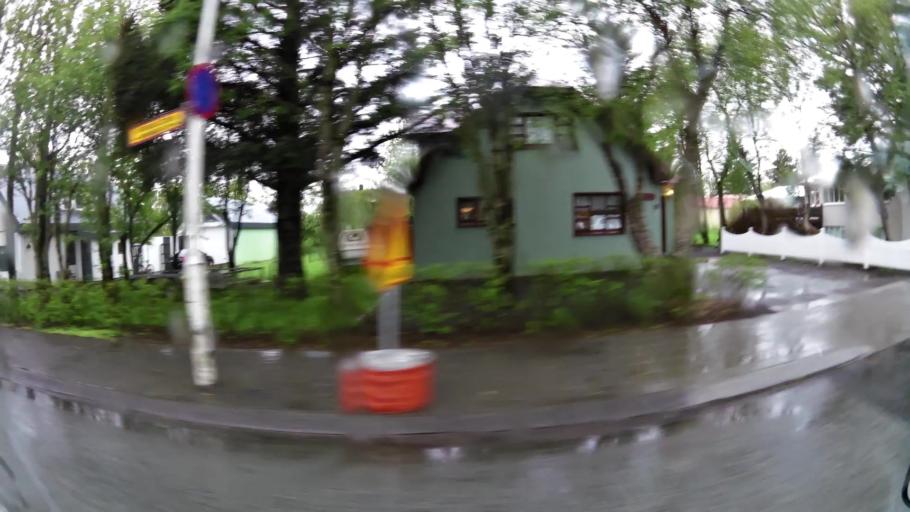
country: IS
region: South
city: Selfoss
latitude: 63.9356
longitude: -20.9991
